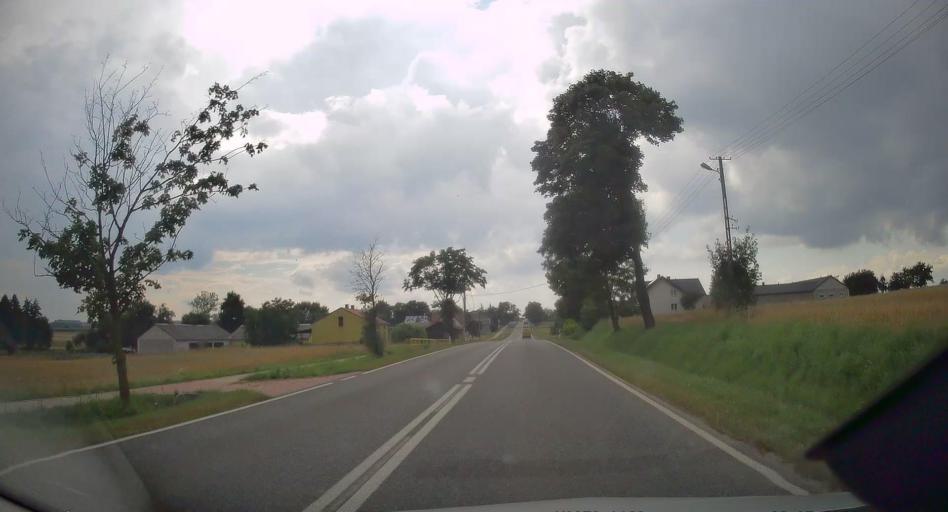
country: PL
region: Lodz Voivodeship
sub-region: Powiat rawski
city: Rawa Mazowiecka
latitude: 51.7726
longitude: 20.1672
